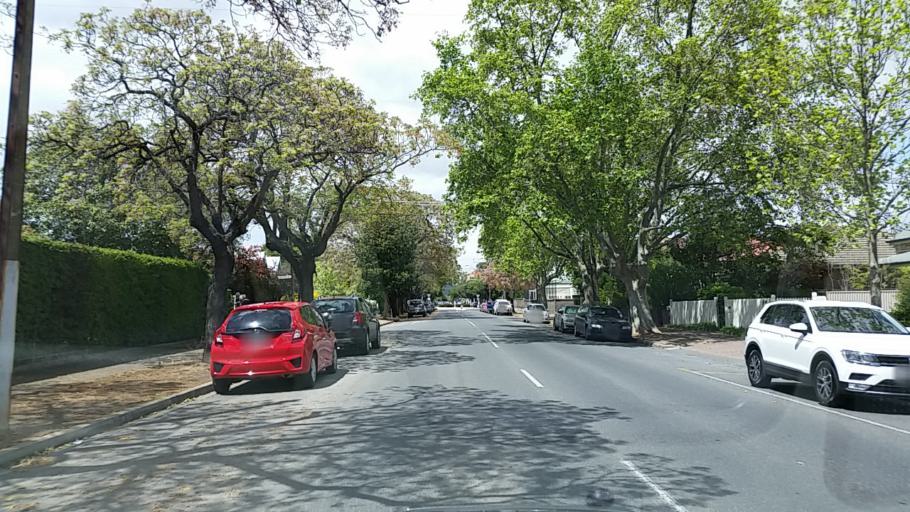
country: AU
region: South Australia
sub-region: Norwood Payneham St Peters
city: Trinity Gardens
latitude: -34.9166
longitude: 138.6363
